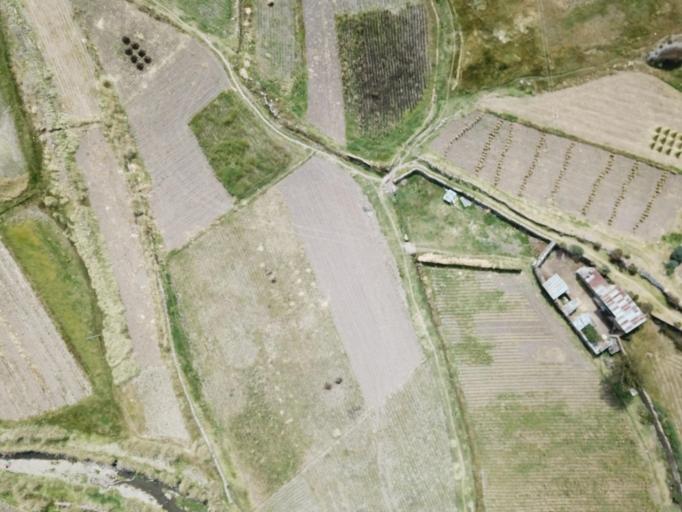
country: BO
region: La Paz
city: Achacachi
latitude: -16.0573
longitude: -68.8108
